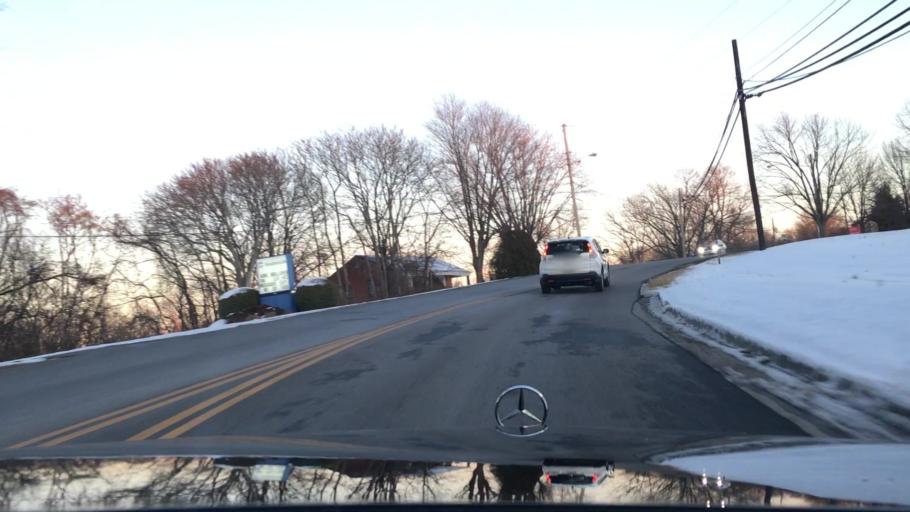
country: US
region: Virginia
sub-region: City of Lynchburg
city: West Lynchburg
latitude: 37.3616
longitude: -79.1944
